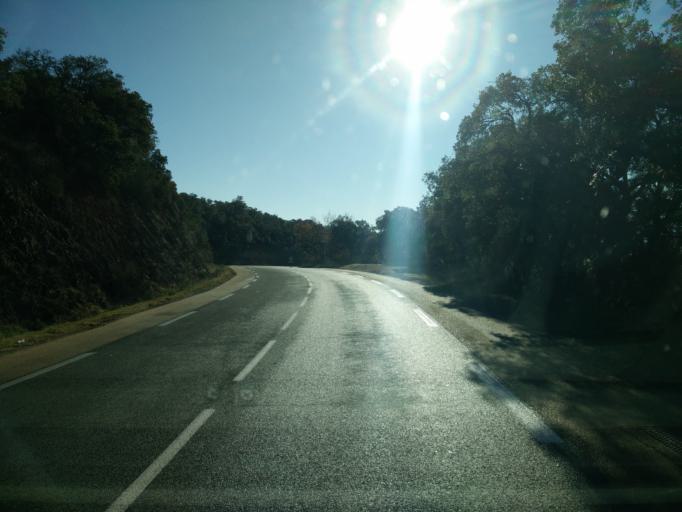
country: FR
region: Provence-Alpes-Cote d'Azur
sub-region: Departement du Var
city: Grimaud
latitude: 43.2771
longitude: 6.5094
